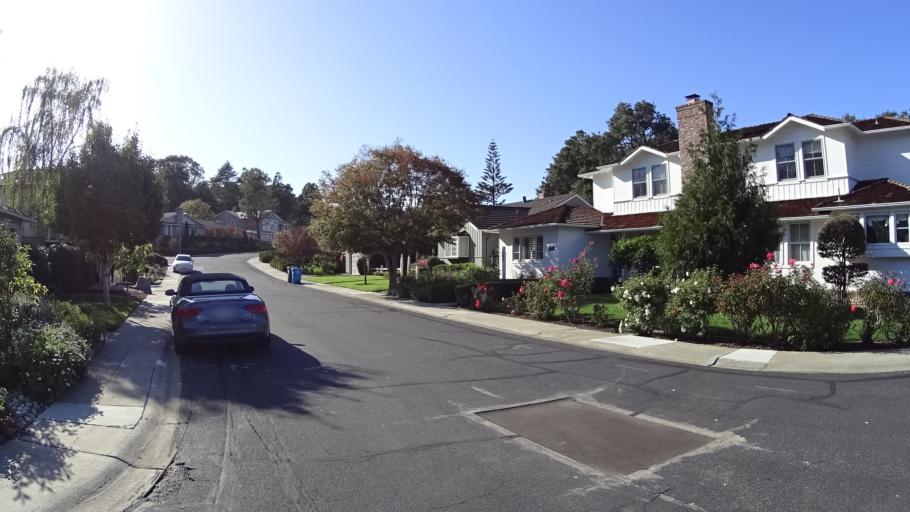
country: US
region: California
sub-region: San Mateo County
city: Hillsborough
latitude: 37.5859
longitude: -122.3834
